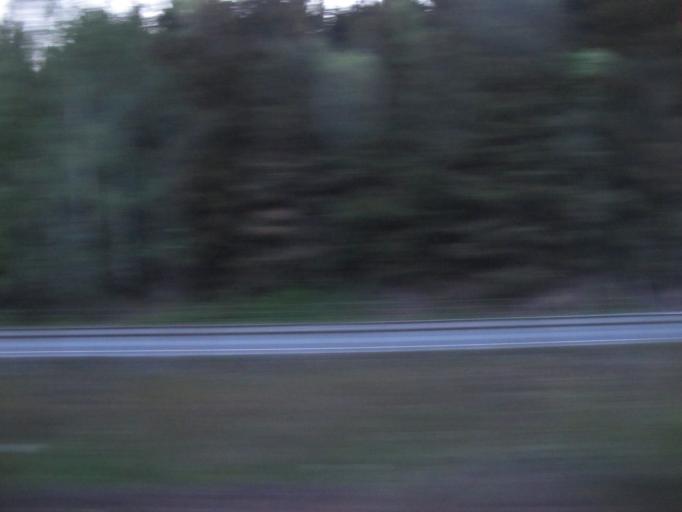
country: NO
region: Oppland
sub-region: Ringebu
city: Ringebu
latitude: 61.5450
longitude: 10.0792
